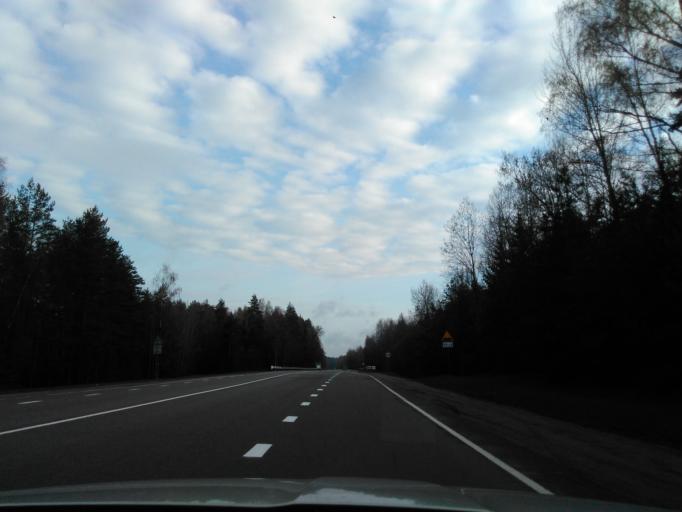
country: BY
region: Minsk
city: Plyeshchanitsy
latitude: 54.3211
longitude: 27.8754
